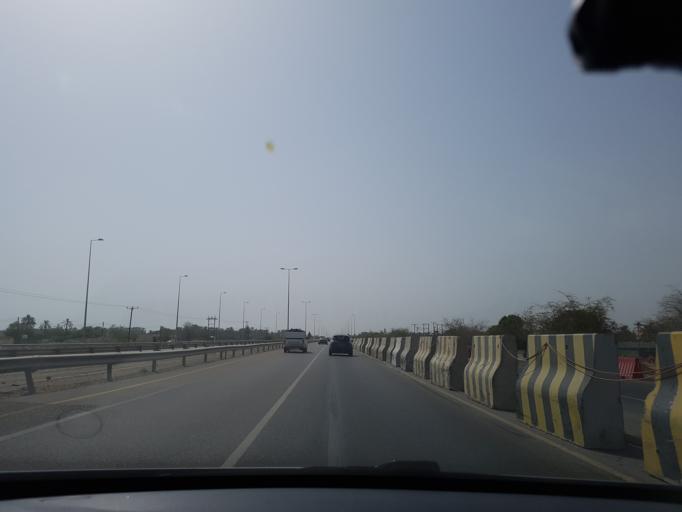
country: OM
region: Al Batinah
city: Al Khaburah
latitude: 23.9969
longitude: 57.0626
